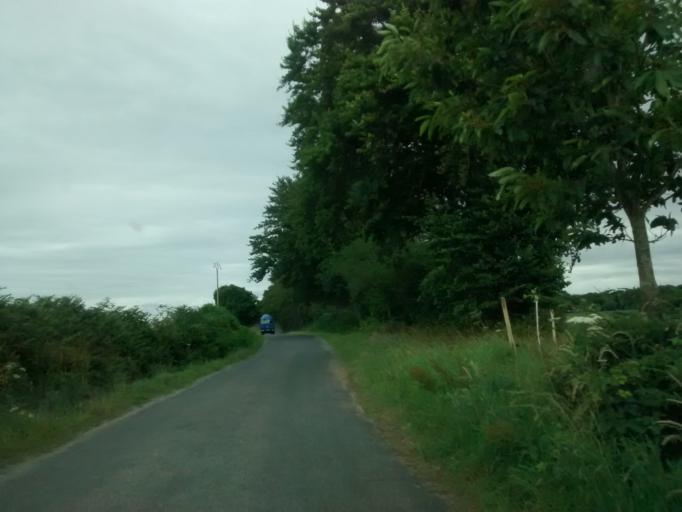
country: FR
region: Brittany
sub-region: Departement des Cotes-d'Armor
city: Trelevern
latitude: 48.7871
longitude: -3.3553
